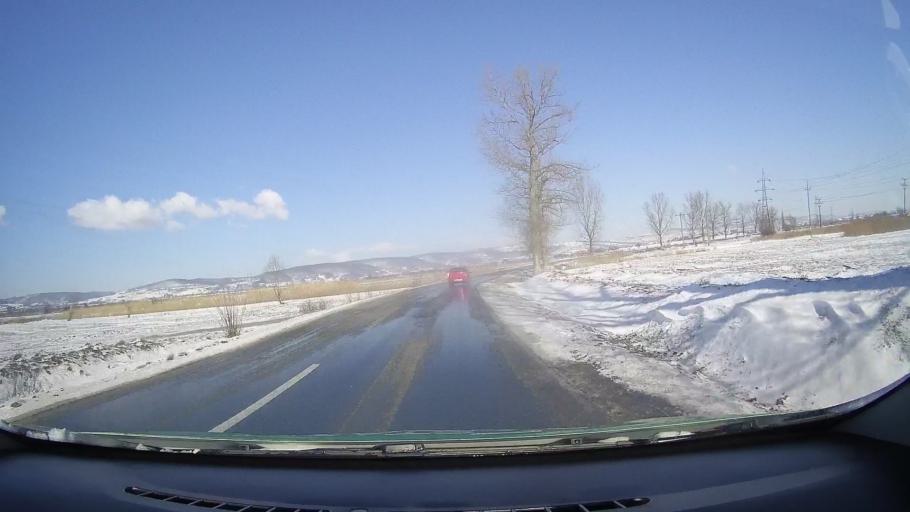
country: RO
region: Sibiu
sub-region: Comuna Avrig
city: Marsa
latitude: 45.7101
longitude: 24.3689
